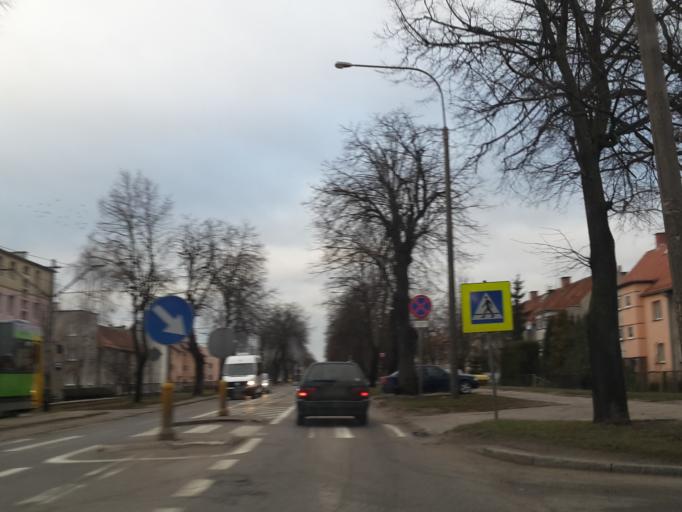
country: PL
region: Warmian-Masurian Voivodeship
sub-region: Powiat elblaski
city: Gronowo Gorne
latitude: 54.1454
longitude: 19.4388
